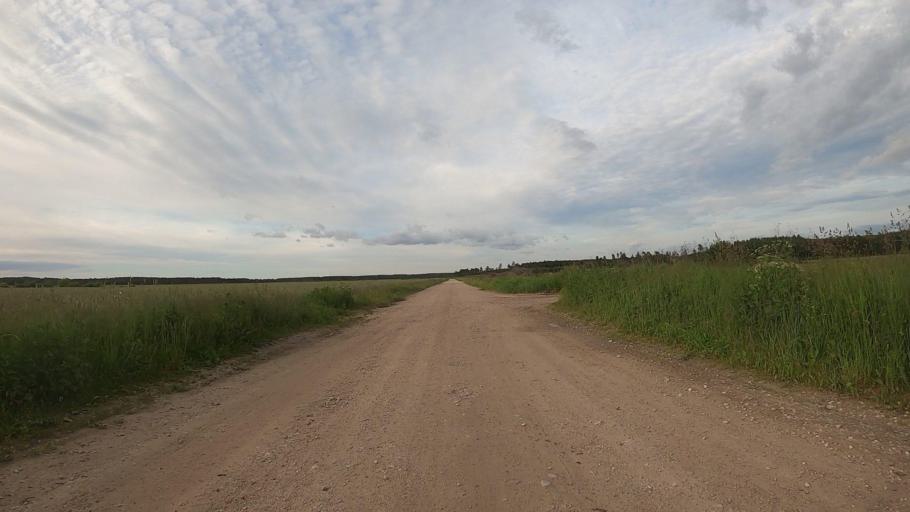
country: LV
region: Olaine
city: Olaine
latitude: 56.8131
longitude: 23.9458
